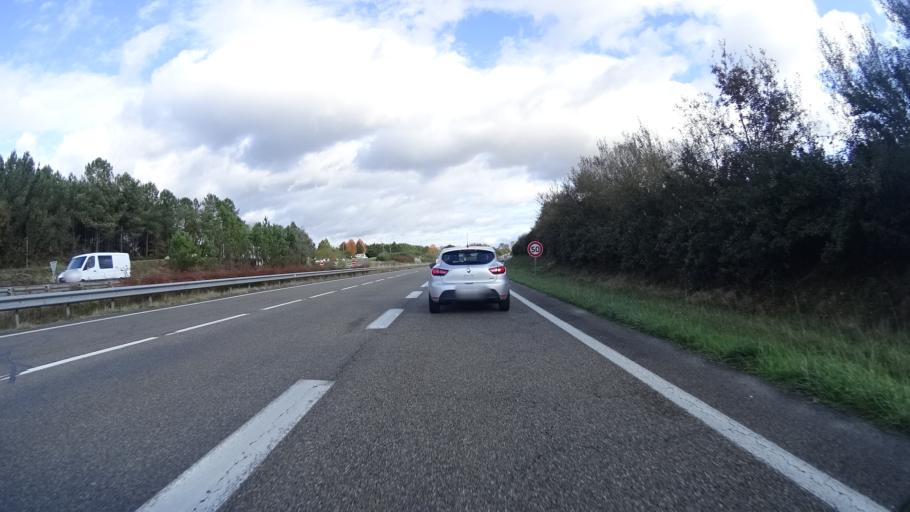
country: FR
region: Aquitaine
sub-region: Departement des Landes
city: Saint-Paul-les-Dax
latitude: 43.7443
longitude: -1.0588
